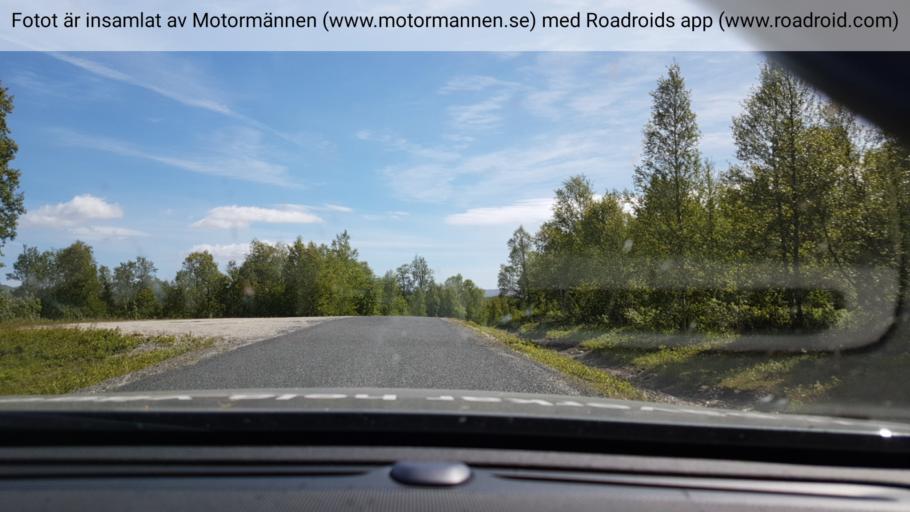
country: NO
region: Nordland
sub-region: Hattfjelldal
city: Hattfjelldal
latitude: 65.3475
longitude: 15.0904
